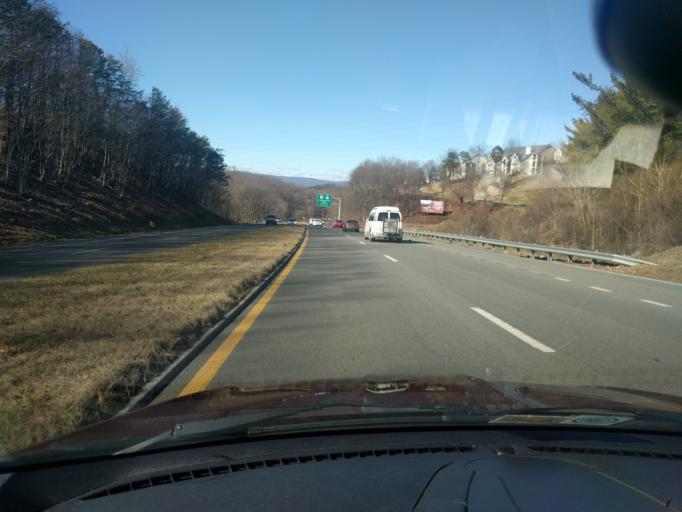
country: US
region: Virginia
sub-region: Roanoke County
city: Narrows
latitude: 37.2160
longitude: -79.9609
